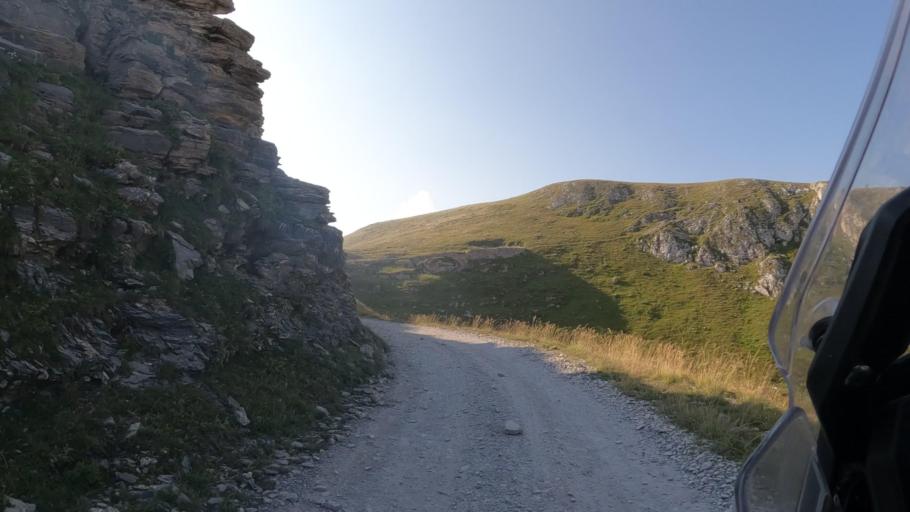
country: IT
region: Piedmont
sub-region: Provincia di Cuneo
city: Limone Piemonte
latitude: 44.1713
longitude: 7.6464
